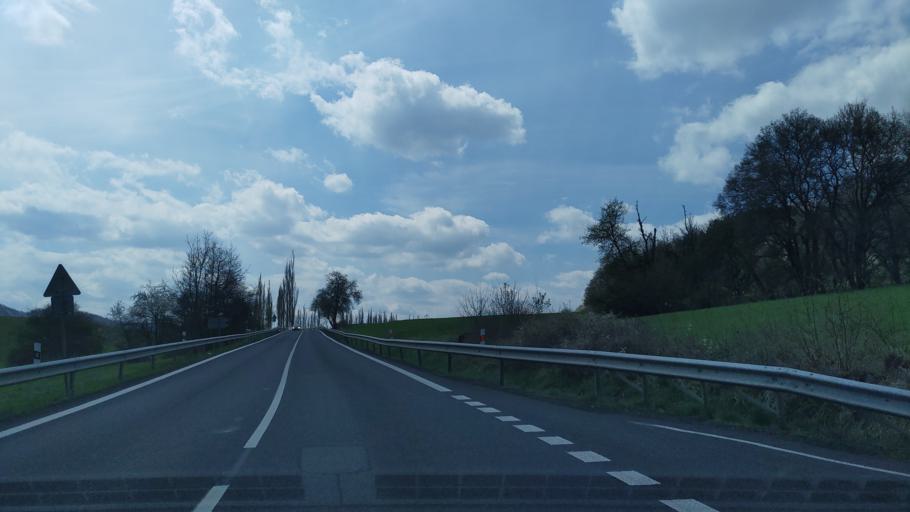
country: CZ
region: Ustecky
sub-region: Okres Chomutov
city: Perstejn
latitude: 50.3369
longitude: 13.0292
